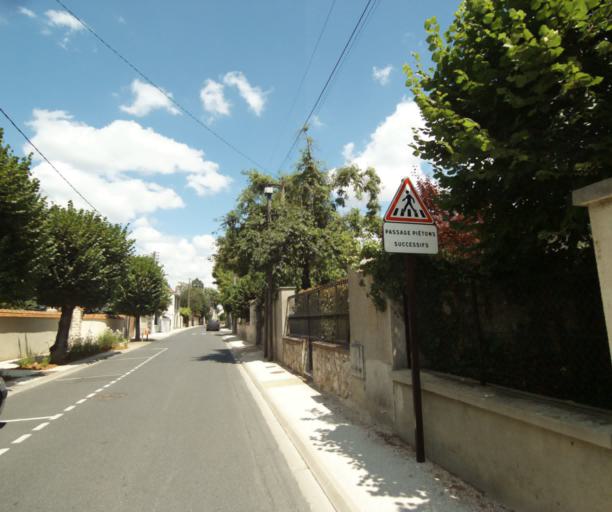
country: FR
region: Ile-de-France
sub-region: Departement de Seine-et-Marne
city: Hericy
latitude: 48.4450
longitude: 2.7606
